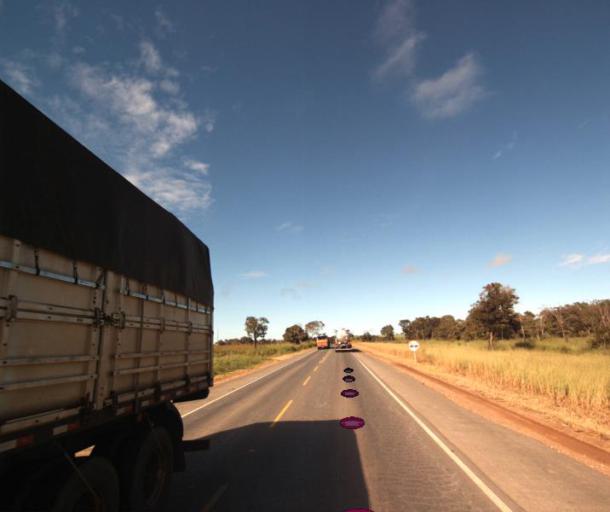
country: BR
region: Goias
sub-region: Itapaci
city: Itapaci
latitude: -14.8363
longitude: -49.3077
